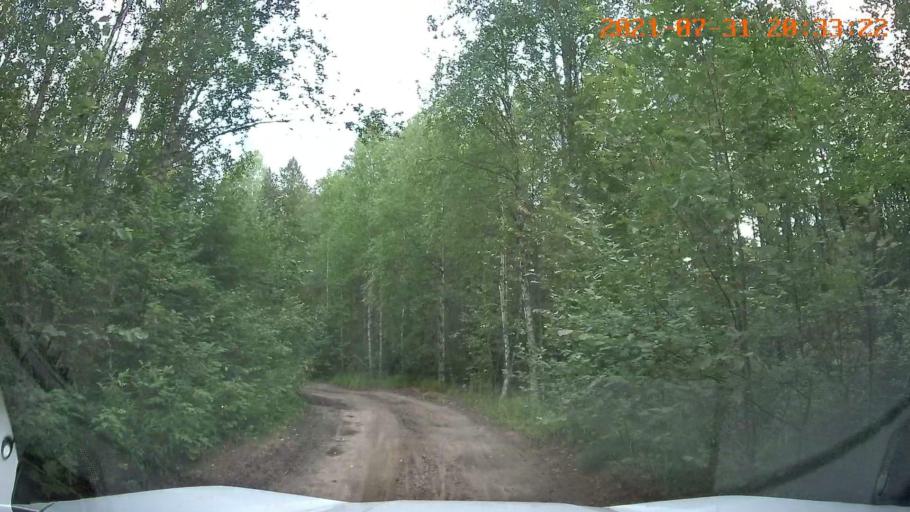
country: RU
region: Republic of Karelia
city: Shal'skiy
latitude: 61.6619
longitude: 36.2690
